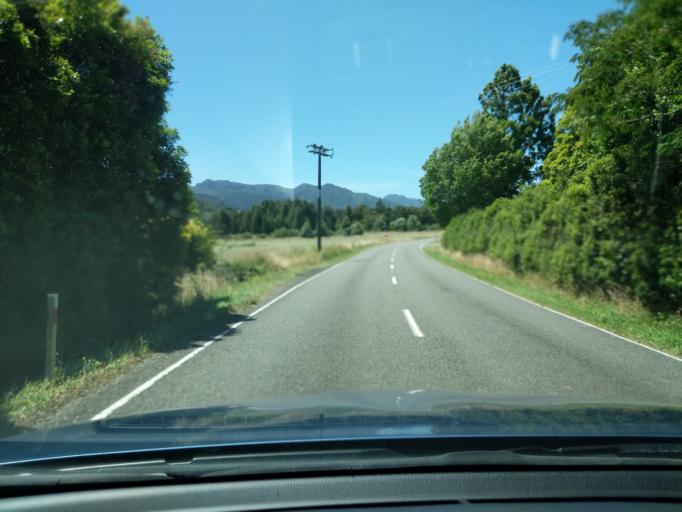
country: NZ
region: Tasman
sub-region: Tasman District
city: Takaka
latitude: -40.7505
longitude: 172.5628
